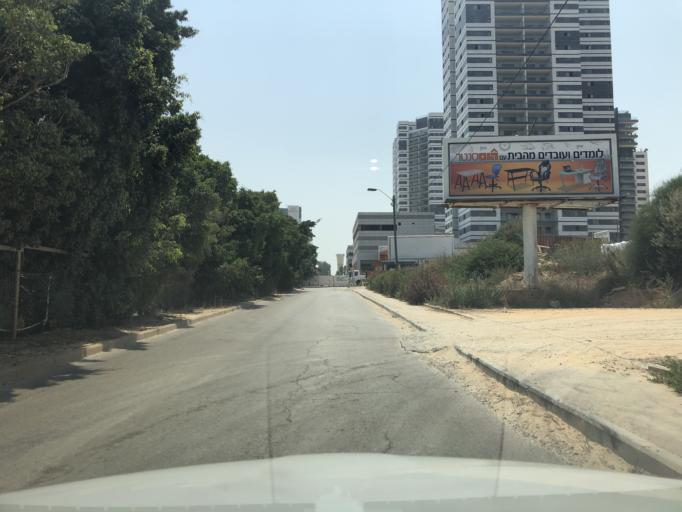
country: IL
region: Central District
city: Ganne Tiqwa
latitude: 32.0671
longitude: 34.8760
